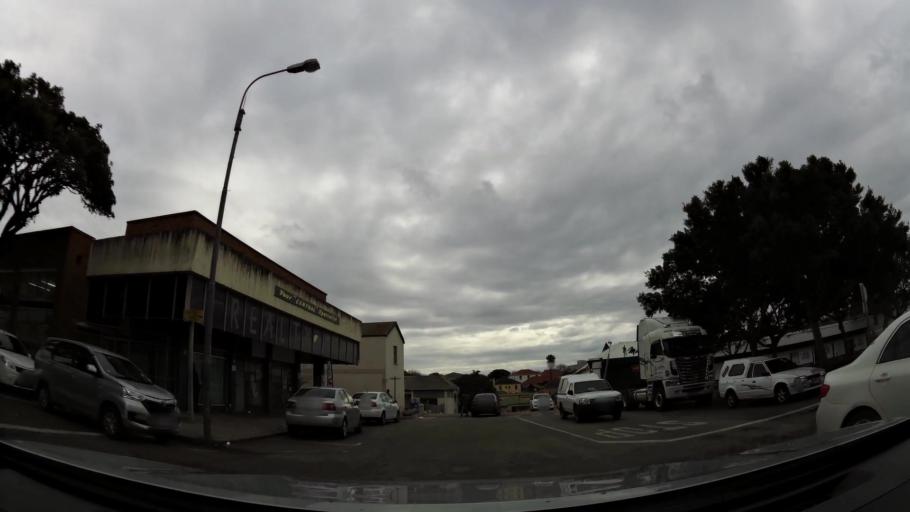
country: ZA
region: Eastern Cape
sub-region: Nelson Mandela Bay Metropolitan Municipality
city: Port Elizabeth
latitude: -33.9622
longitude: 25.6143
